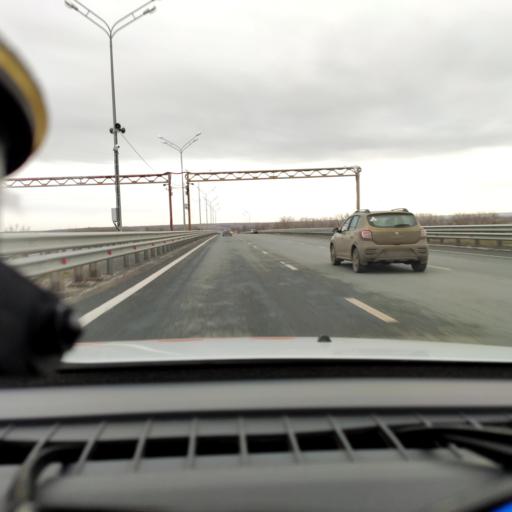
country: RU
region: Samara
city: Smyshlyayevka
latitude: 53.1781
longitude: 50.3088
